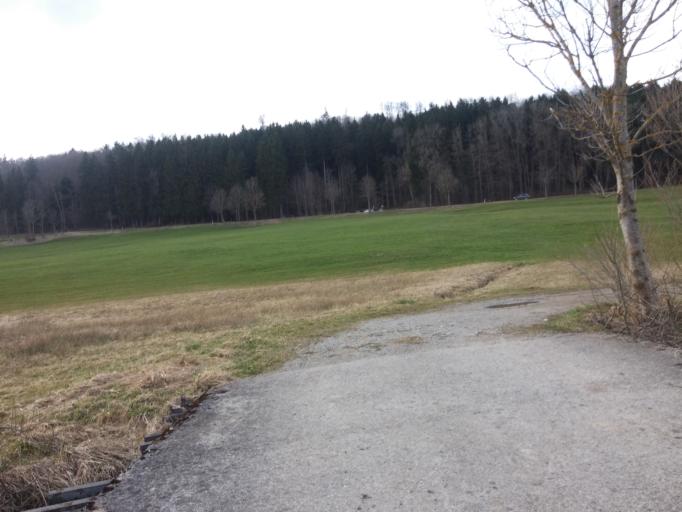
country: DE
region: Bavaria
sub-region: Swabia
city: Wildpoldsried
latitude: 47.7668
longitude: 10.3898
